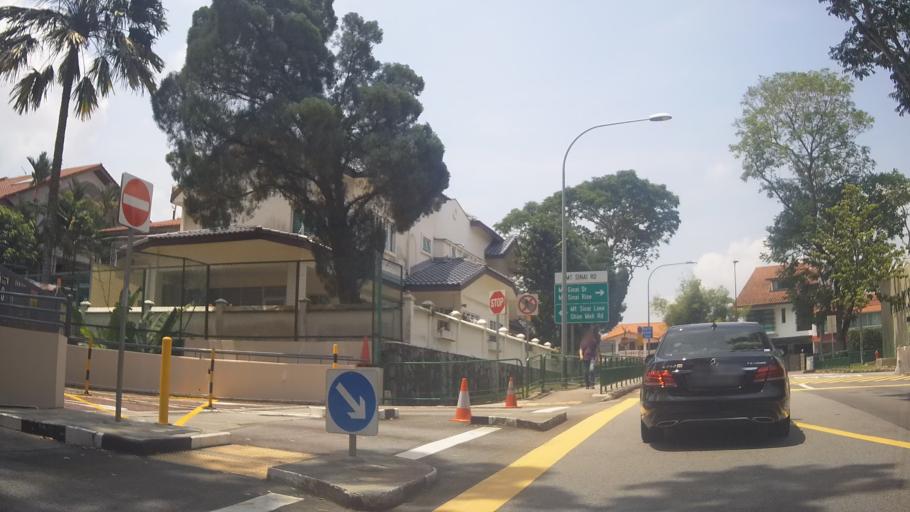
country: SG
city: Singapore
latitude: 1.3159
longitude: 103.7837
